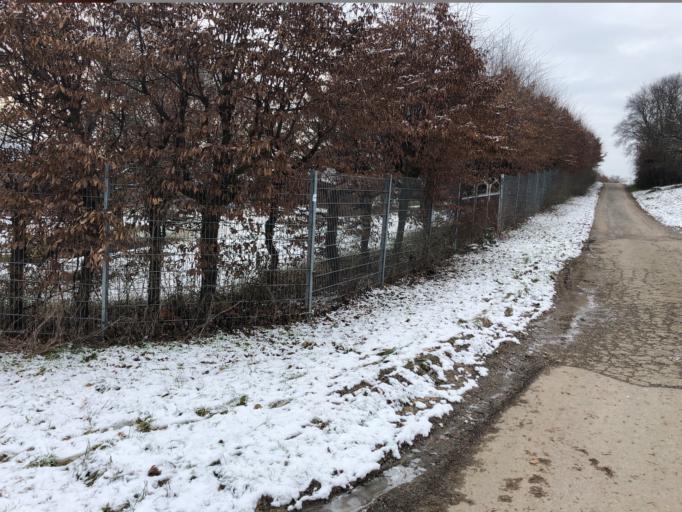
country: DE
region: Baden-Wuerttemberg
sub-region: Tuebingen Region
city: Nehren
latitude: 48.4151
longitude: 9.0704
